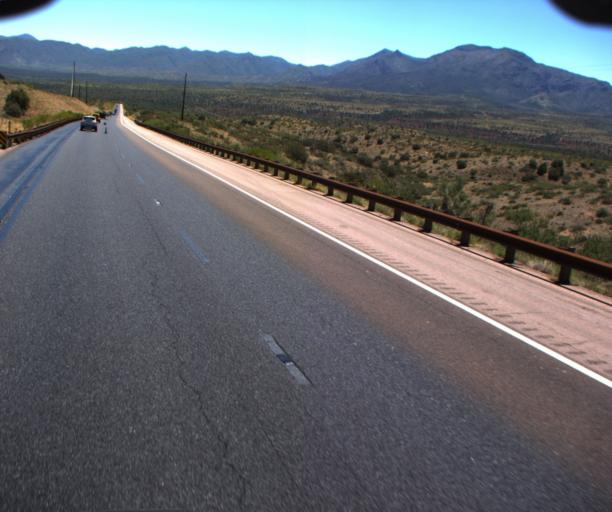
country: US
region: Arizona
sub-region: Gila County
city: Payson
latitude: 34.1389
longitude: -111.3519
